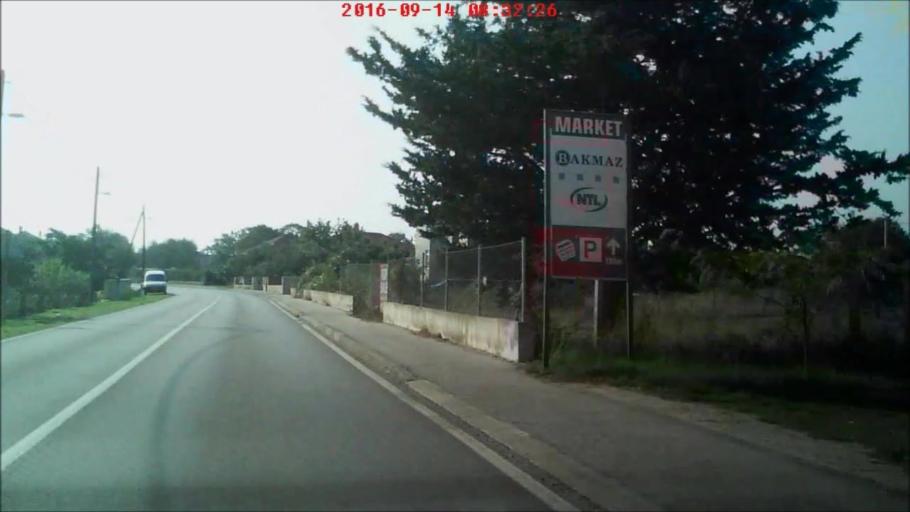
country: HR
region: Zadarska
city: Policnik
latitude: 44.1632
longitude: 15.3060
